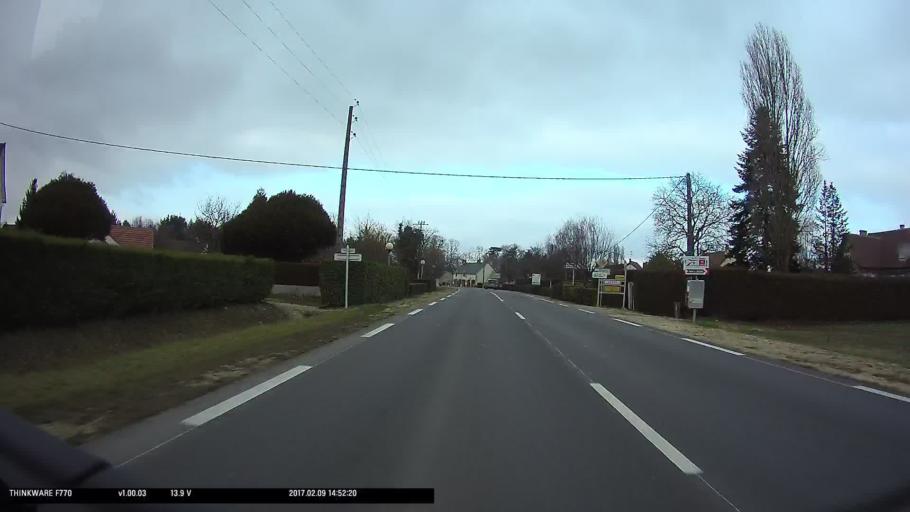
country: FR
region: Centre
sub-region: Departement du Cher
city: Levet
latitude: 46.9209
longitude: 2.4108
